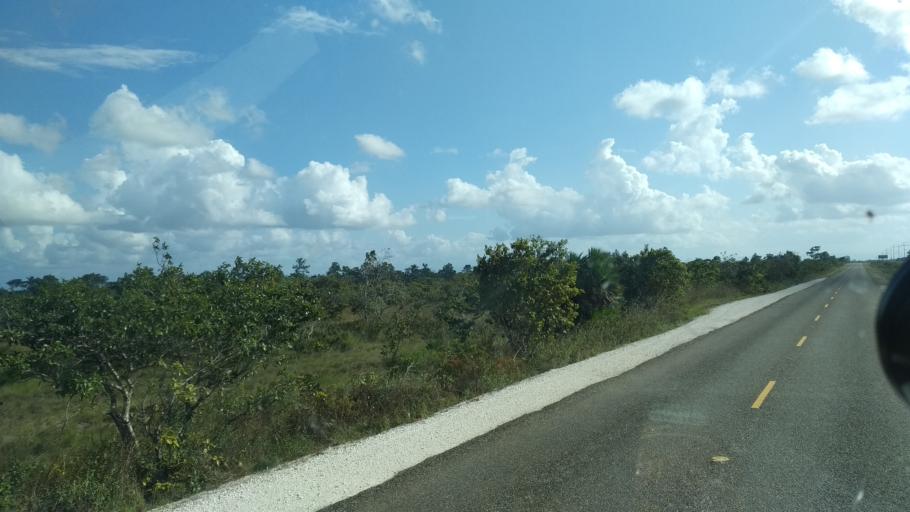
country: BZ
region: Cayo
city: Belmopan
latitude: 17.3936
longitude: -88.5112
